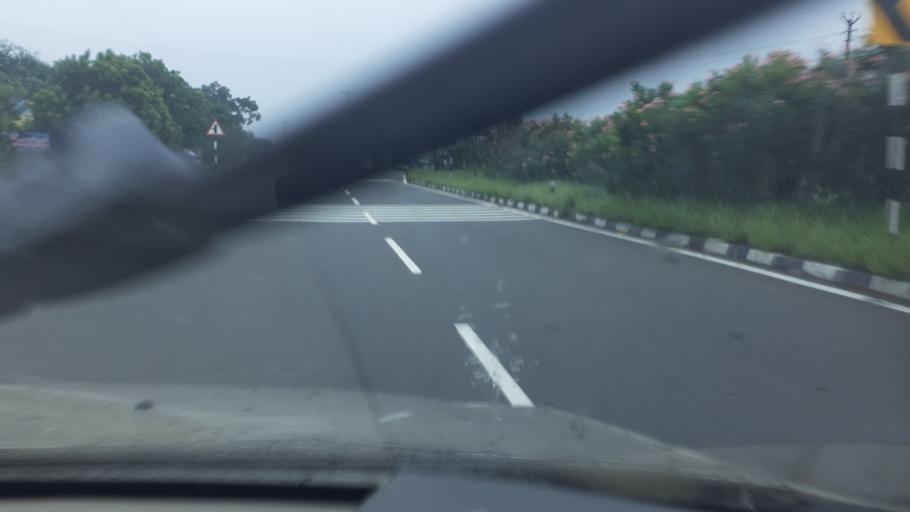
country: IN
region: Tamil Nadu
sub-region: Virudhunagar
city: Virudunagar
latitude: 9.6253
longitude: 77.9585
